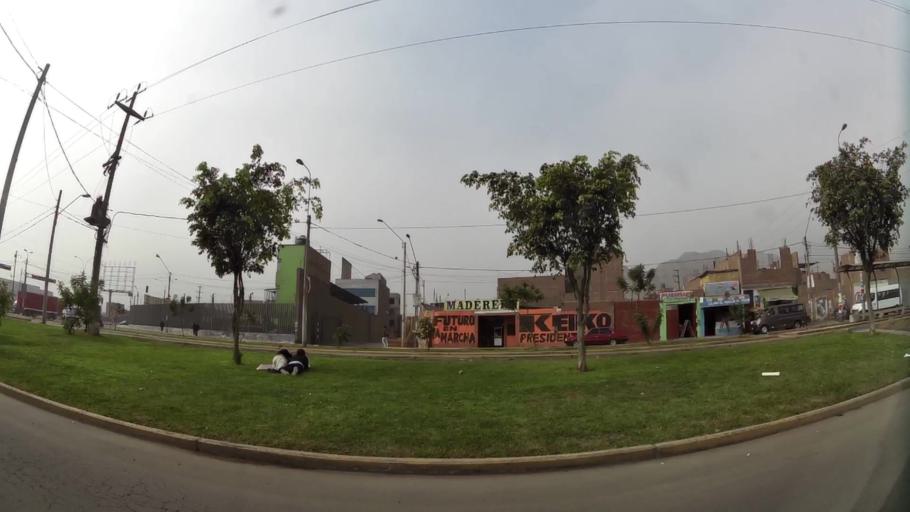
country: PE
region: Lima
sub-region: Lima
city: Santa Maria
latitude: -11.9973
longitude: -76.8346
